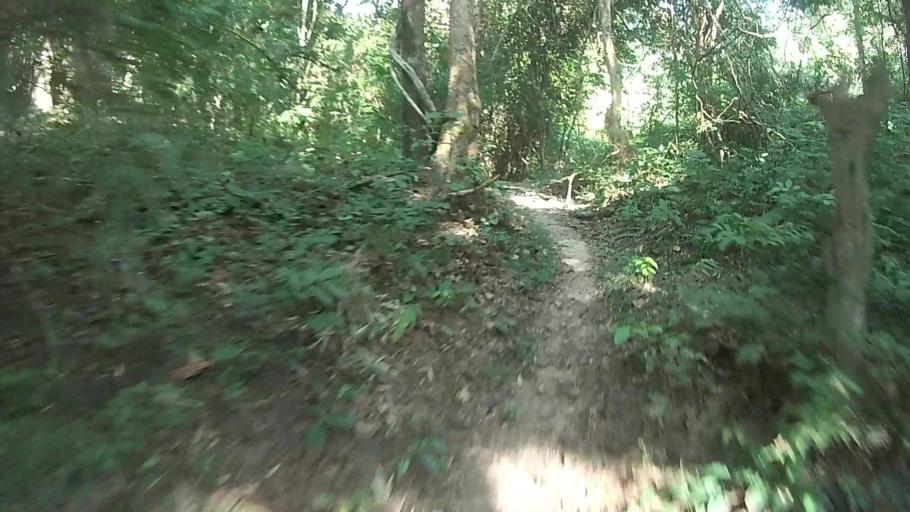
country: TH
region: Chiang Mai
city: San Sai
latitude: 18.9554
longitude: 99.0643
